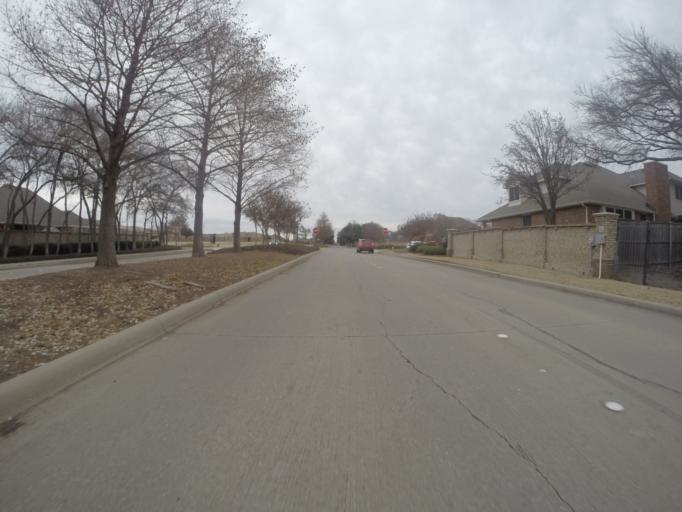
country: US
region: Texas
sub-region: Collin County
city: Saint Paul
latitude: 33.0273
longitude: -96.5686
